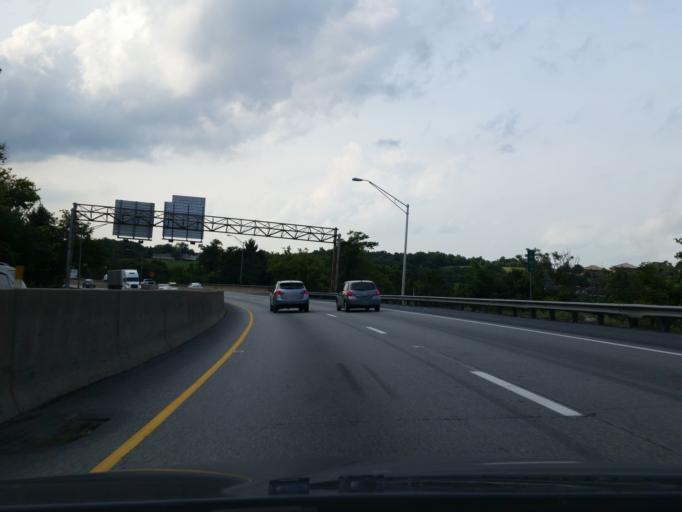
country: US
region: Pennsylvania
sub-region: Dauphin County
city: Lawnton
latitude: 40.2567
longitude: -76.8103
